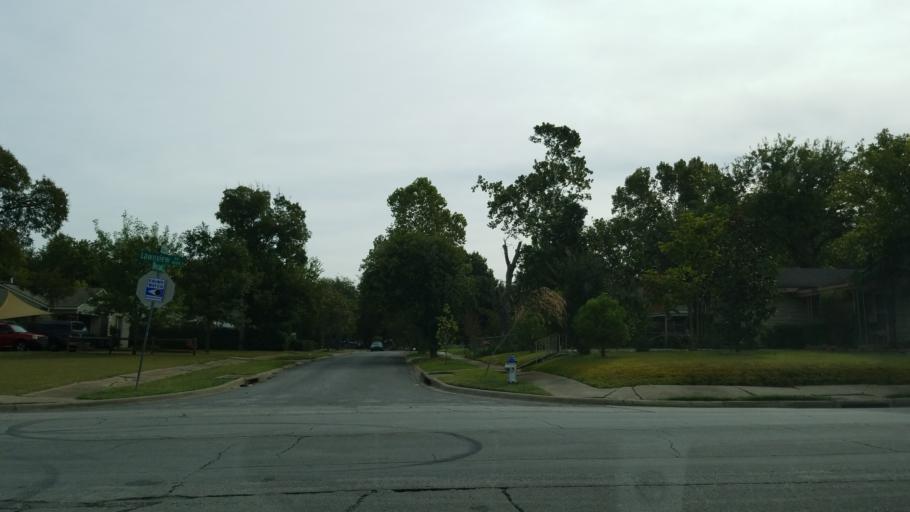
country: US
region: Texas
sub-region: Dallas County
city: Dallas
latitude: 32.7726
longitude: -96.7184
